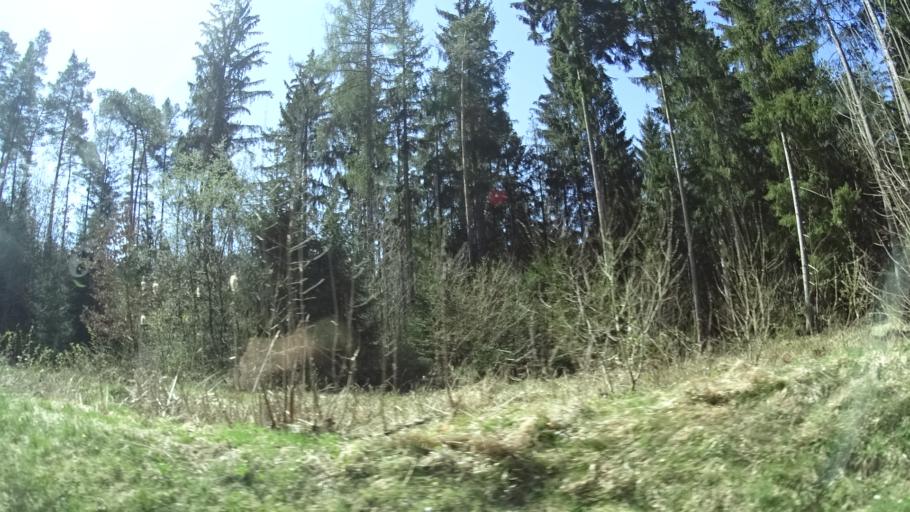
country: DE
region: Bavaria
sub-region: Upper Palatinate
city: Kastl
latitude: 49.3836
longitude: 11.6914
